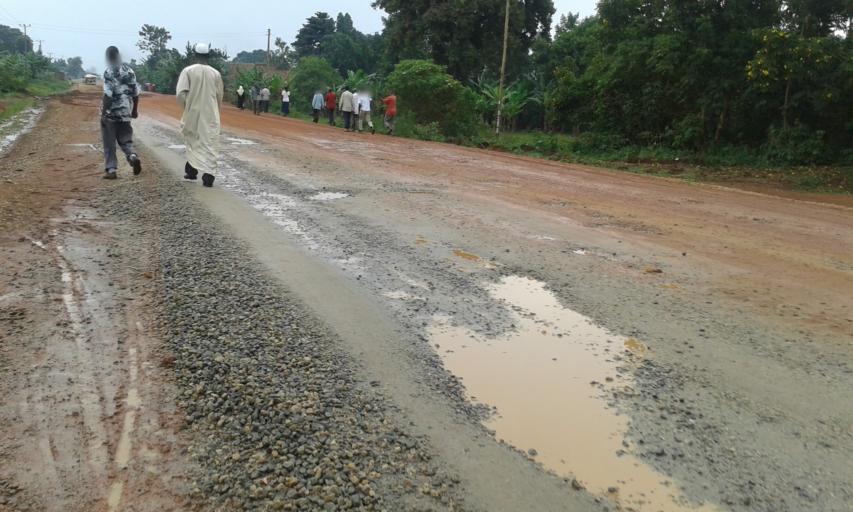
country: UG
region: Eastern Region
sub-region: Mbale District
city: Mbale
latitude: 1.1430
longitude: 34.1904
